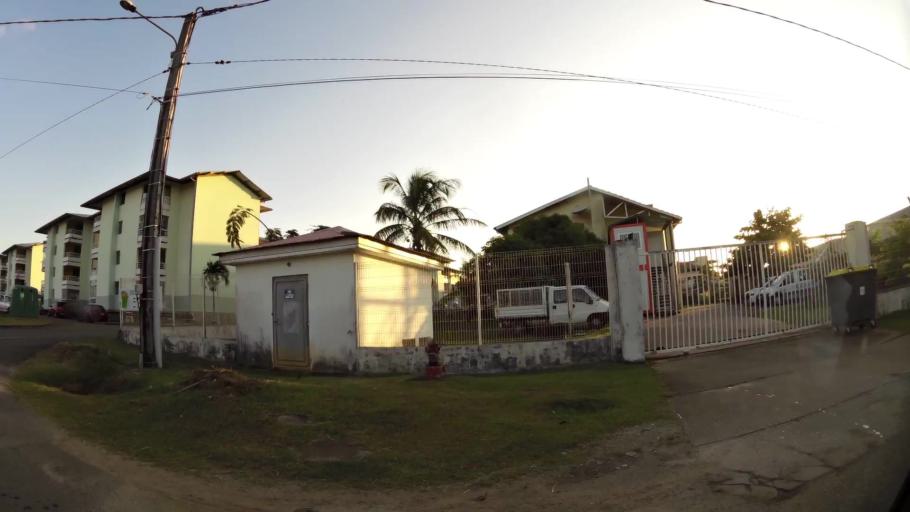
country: GF
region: Guyane
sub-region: Guyane
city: Cayenne
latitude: 4.9281
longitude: -52.3040
